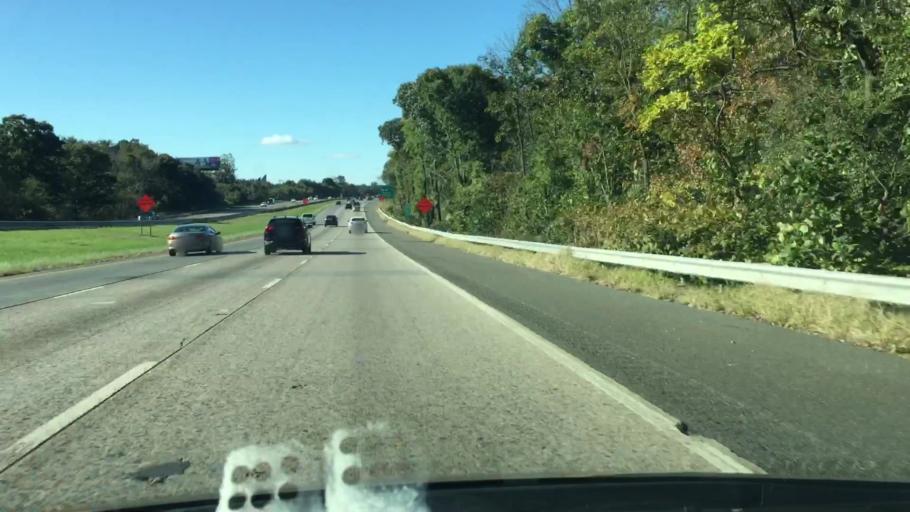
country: US
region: New Jersey
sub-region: Camden County
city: Blackwood
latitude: 39.8196
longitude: -75.0732
